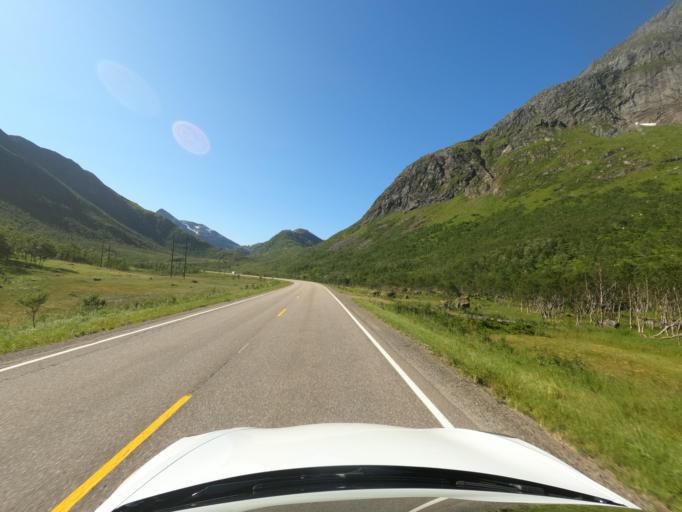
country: NO
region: Nordland
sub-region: Lodingen
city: Lodingen
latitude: 68.4992
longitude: 15.7035
